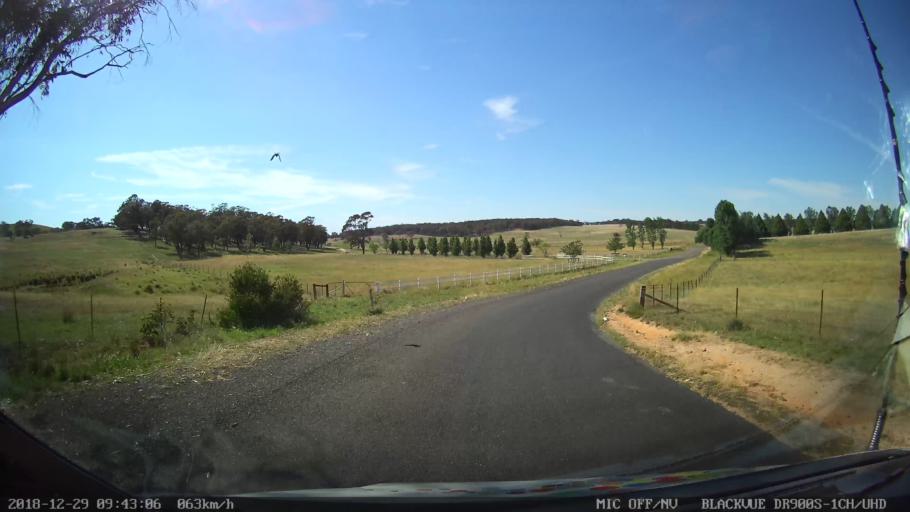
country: AU
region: New South Wales
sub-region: Upper Lachlan Shire
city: Crookwell
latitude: -34.6761
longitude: 149.4246
